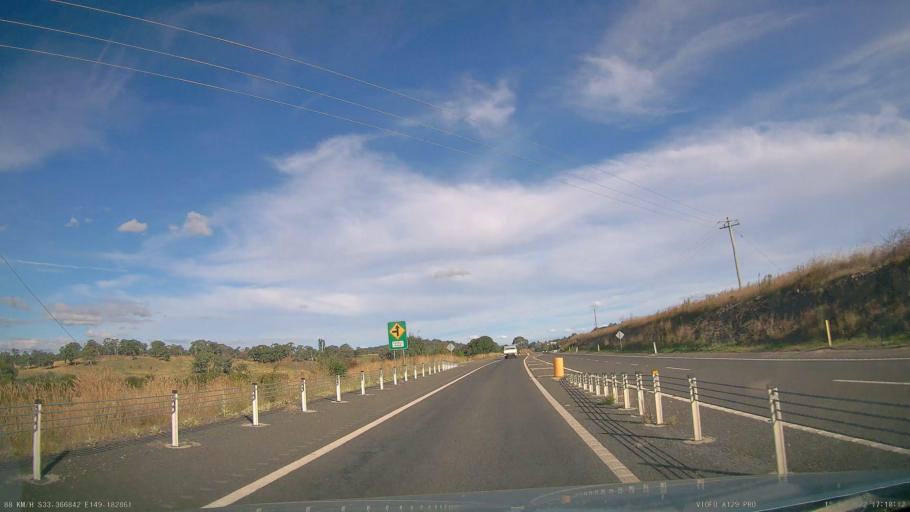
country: AU
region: New South Wales
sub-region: Blayney
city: Millthorpe
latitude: -33.3671
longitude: 149.1831
